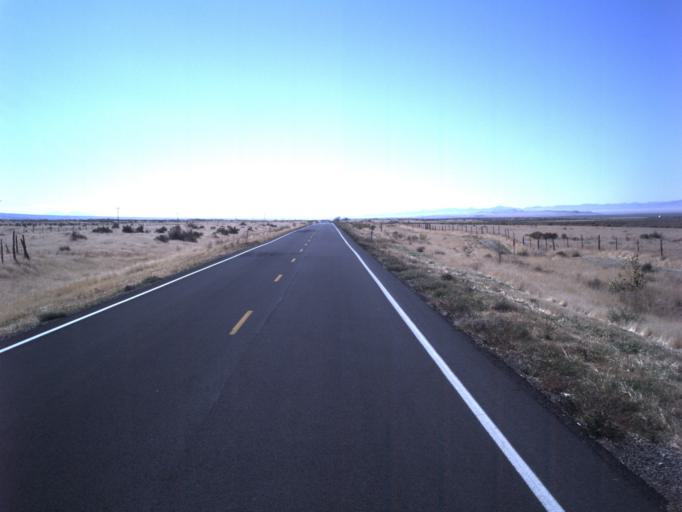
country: US
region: Utah
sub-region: Tooele County
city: Grantsville
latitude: 40.5222
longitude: -112.7477
